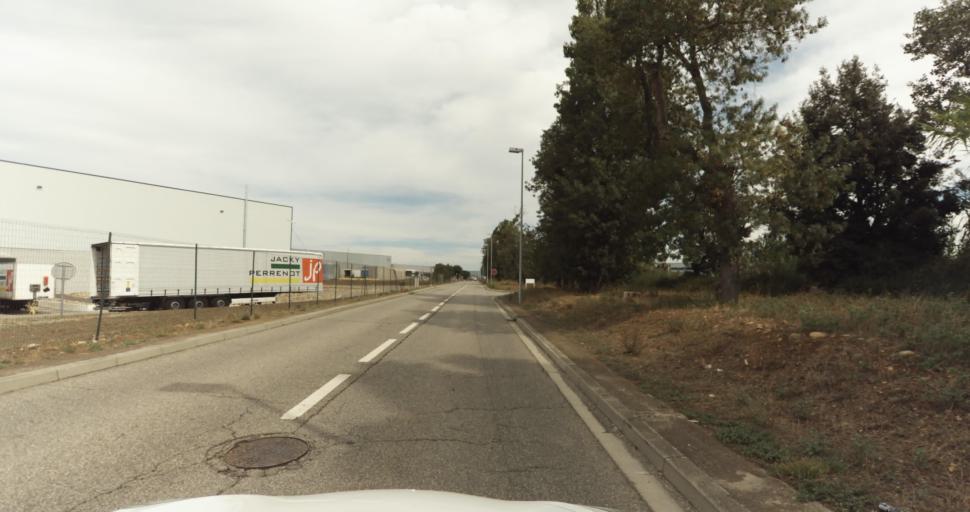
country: FR
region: Provence-Alpes-Cote d'Azur
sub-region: Departement des Bouches-du-Rhone
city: Miramas
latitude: 43.6043
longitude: 4.9995
